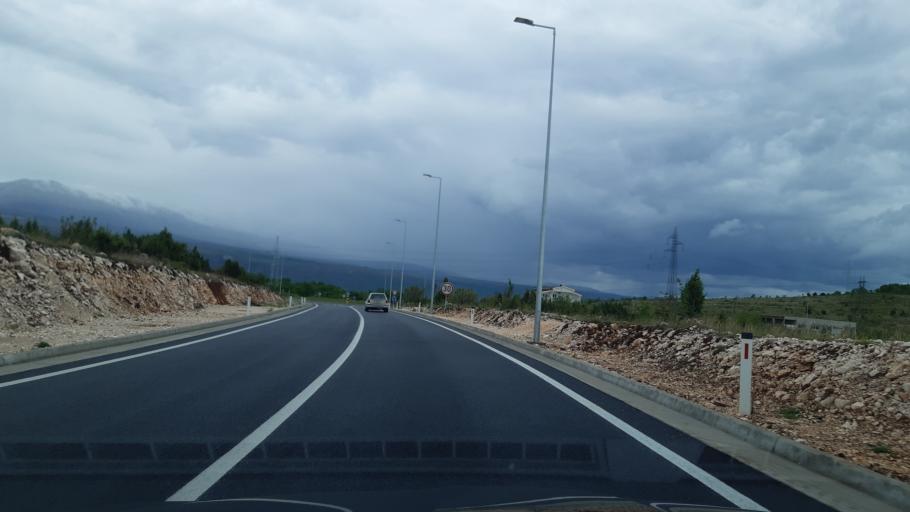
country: BA
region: Federation of Bosnia and Herzegovina
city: Rodoc
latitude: 43.3113
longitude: 17.7715
